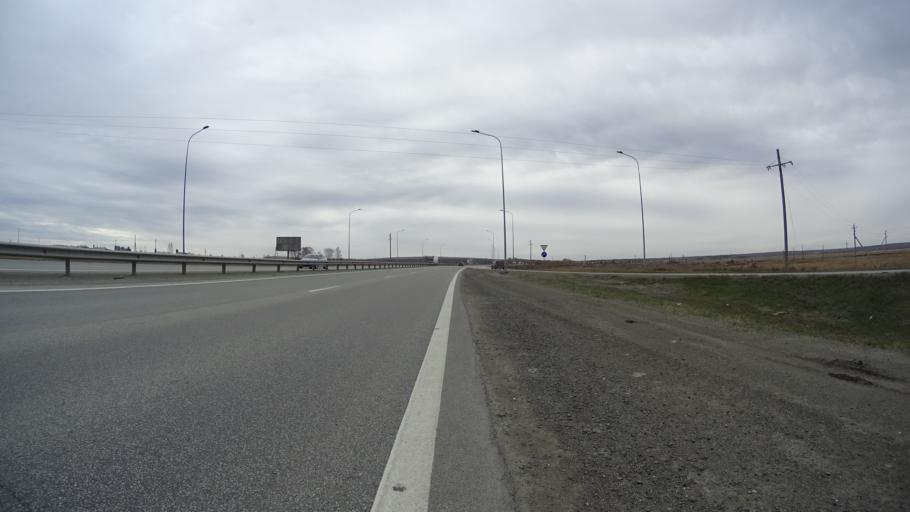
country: RU
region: Chelyabinsk
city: Roza
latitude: 54.9919
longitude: 61.4457
